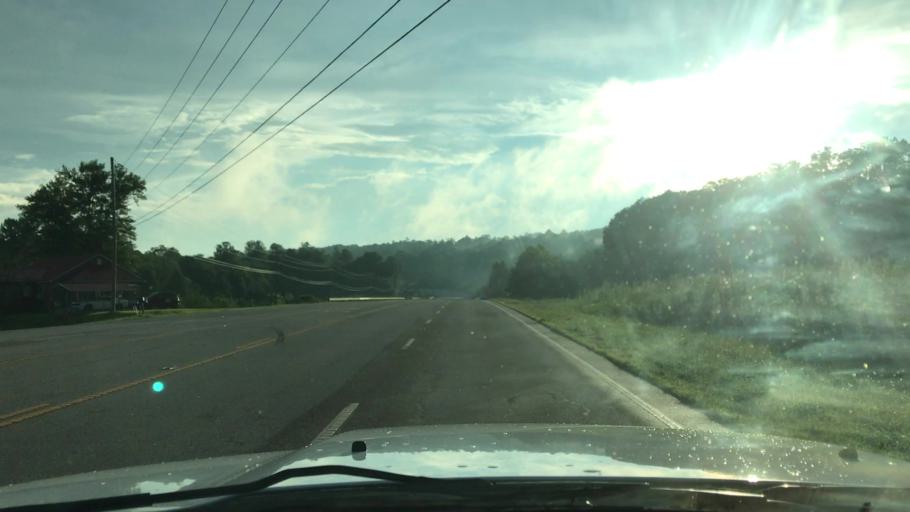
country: US
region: North Carolina
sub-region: Cherokee County
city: Murphy
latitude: 34.9890
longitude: -84.1722
